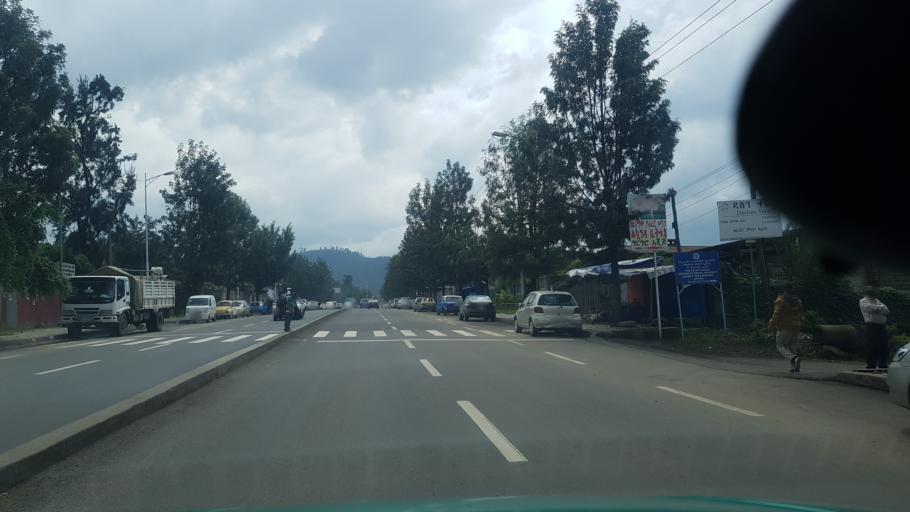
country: ET
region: Adis Abeba
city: Addis Ababa
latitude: 9.0216
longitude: 38.7738
